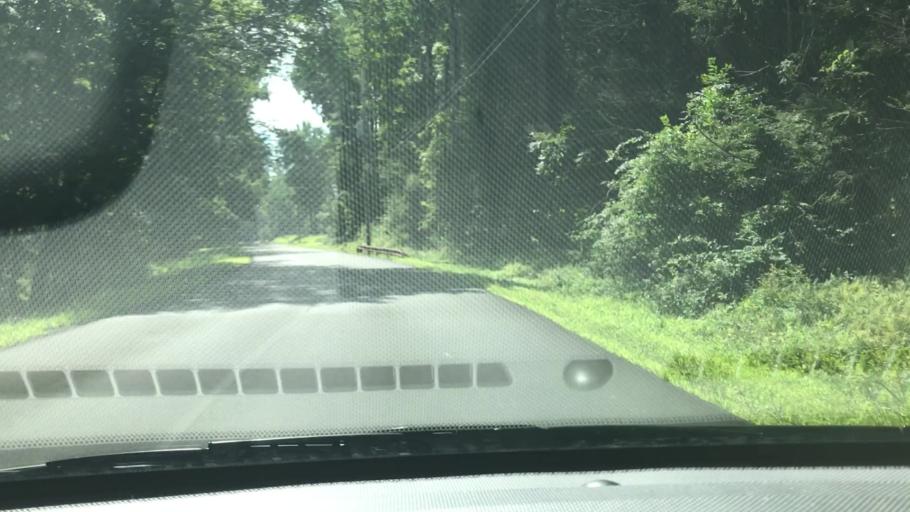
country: US
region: New York
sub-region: Ulster County
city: Shokan
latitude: 41.9579
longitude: -74.2671
